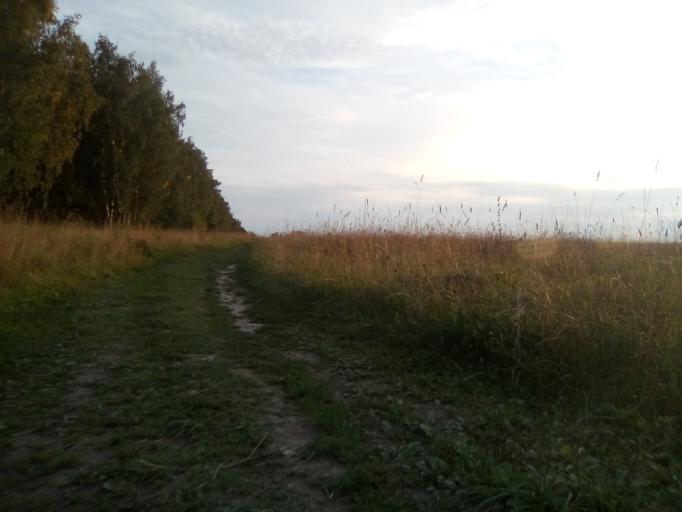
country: RU
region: Moskovskaya
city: Kokoshkino
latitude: 55.6091
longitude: 37.1571
